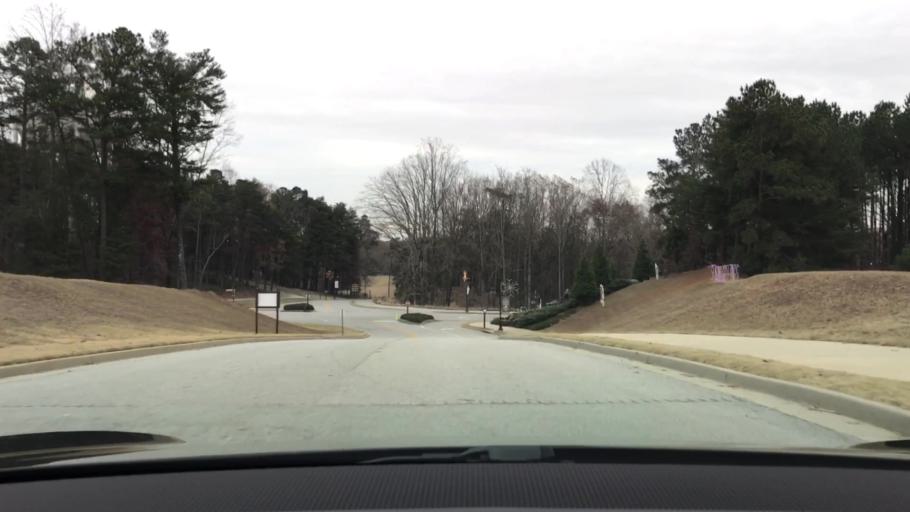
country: US
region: Georgia
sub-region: Gwinnett County
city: Buford
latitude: 34.1767
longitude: -84.0267
